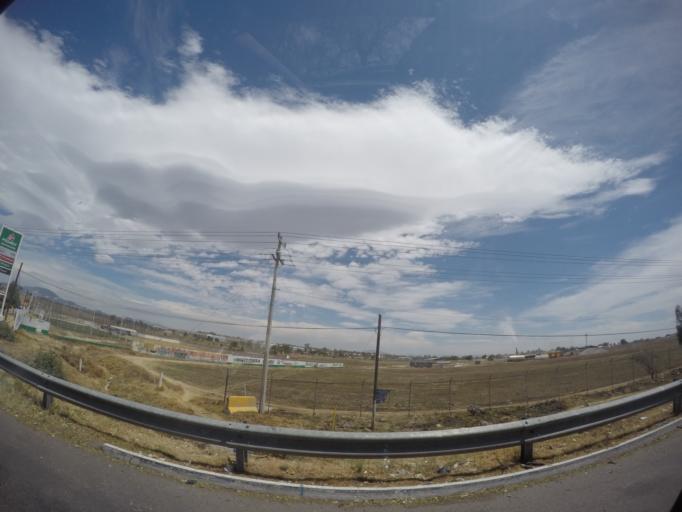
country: MX
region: Mexico
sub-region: Cuautitlan
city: Barrio Tlatenco
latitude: 19.7386
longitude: -99.2113
